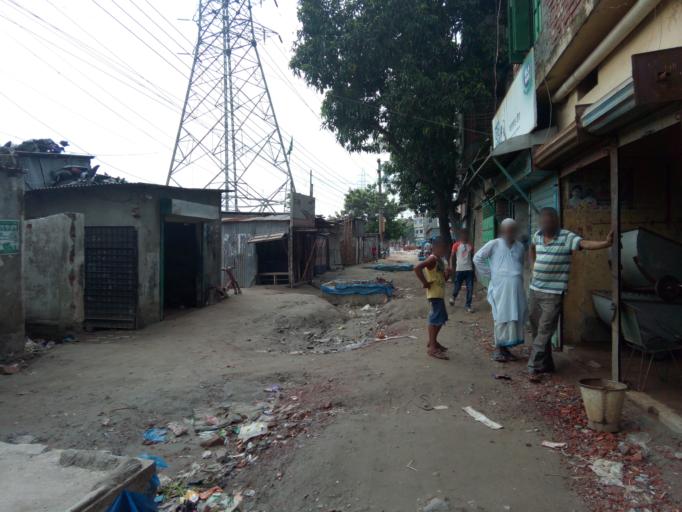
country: BD
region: Dhaka
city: Azimpur
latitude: 23.7169
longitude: 90.3768
